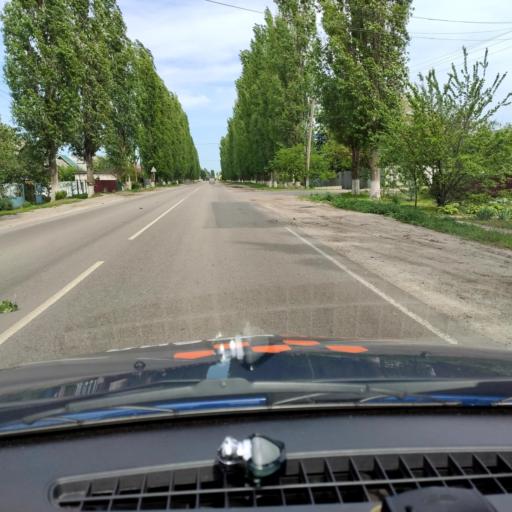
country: RU
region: Voronezj
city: Maslovka
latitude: 51.5365
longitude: 39.3304
